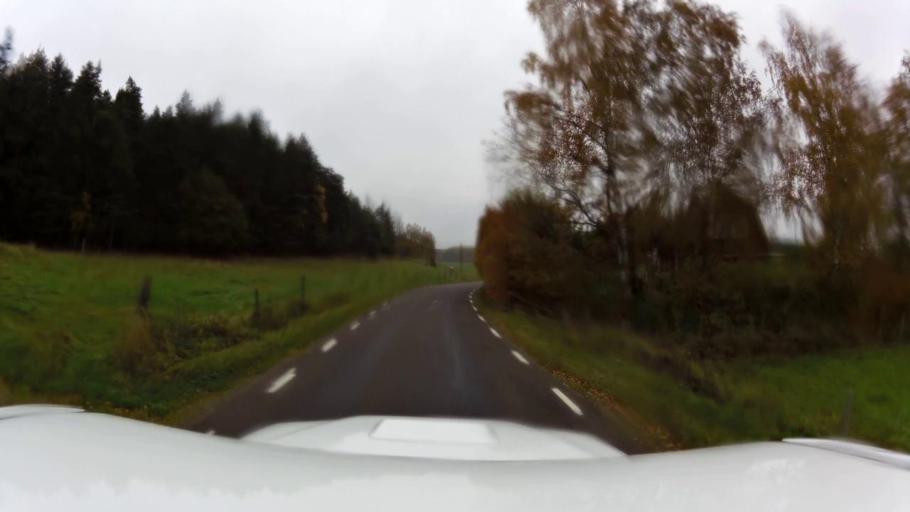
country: SE
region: OEstergoetland
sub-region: Linkopings Kommun
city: Linghem
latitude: 58.3593
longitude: 15.8404
